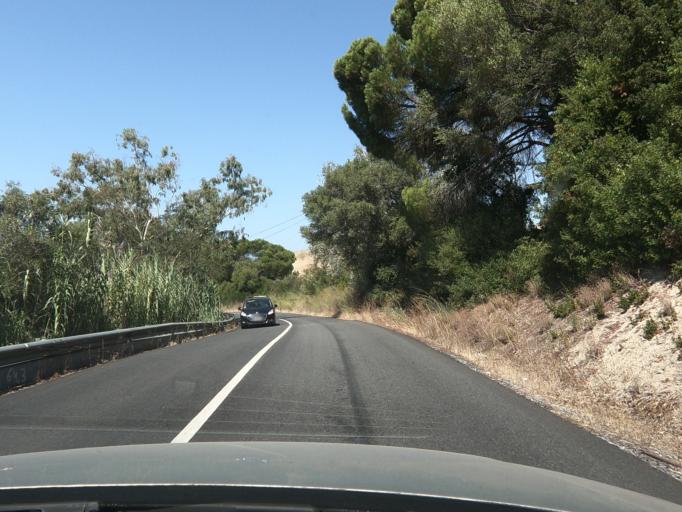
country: PT
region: Setubal
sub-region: Alcacer do Sal
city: Alcacer do Sal
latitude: 38.3570
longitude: -8.4740
